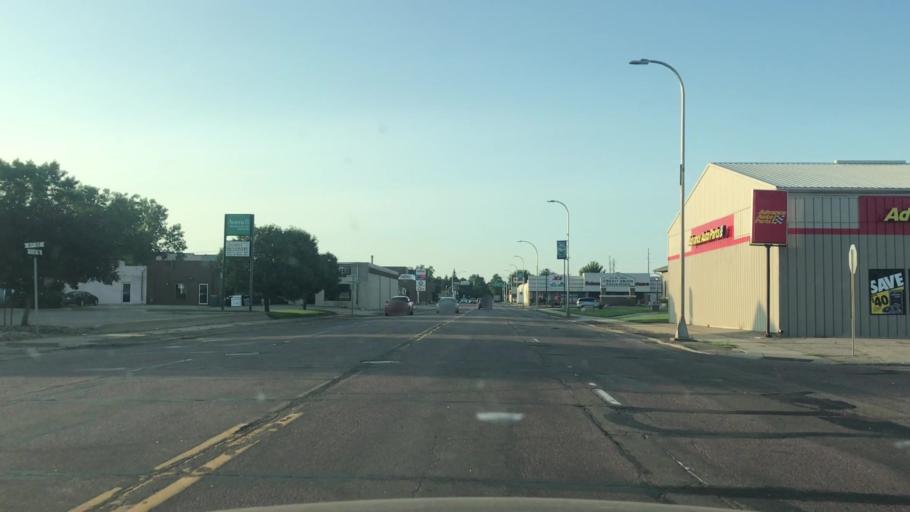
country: US
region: Minnesota
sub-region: Cottonwood County
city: Windom
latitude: 43.8641
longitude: -95.1149
